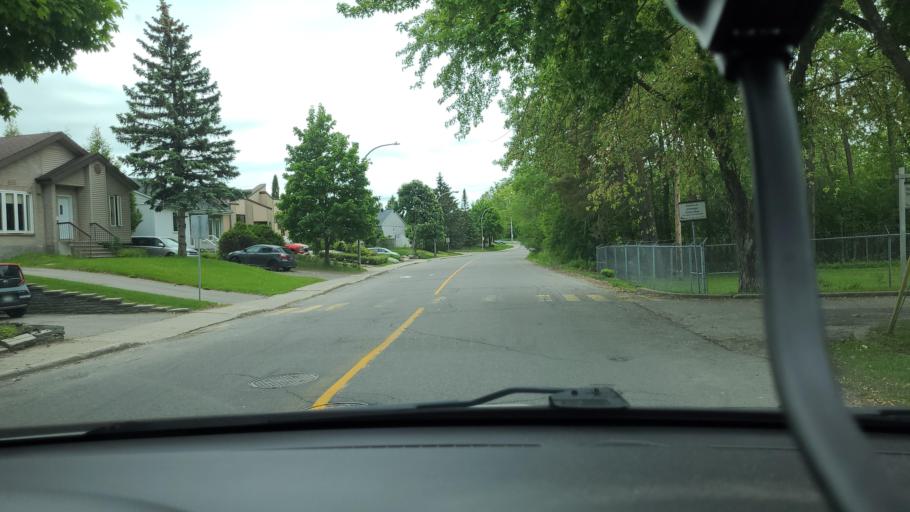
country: CA
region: Quebec
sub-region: Laurentides
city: Rosemere
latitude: 45.6268
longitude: -73.7744
